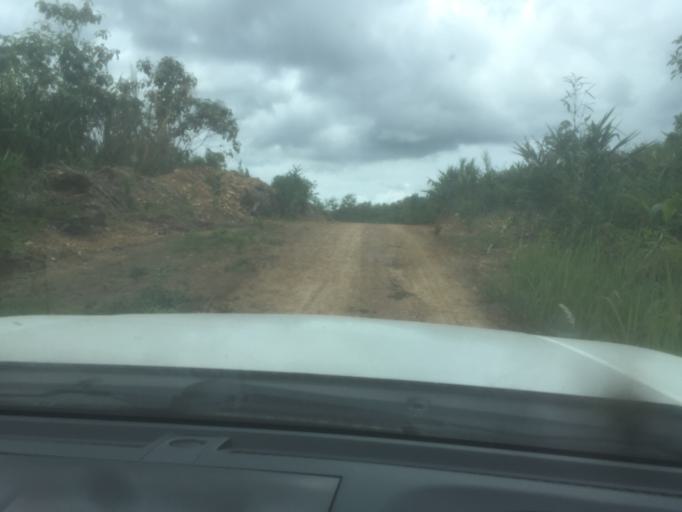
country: LA
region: Phongsali
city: Khoa
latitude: 20.9263
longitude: 102.5417
